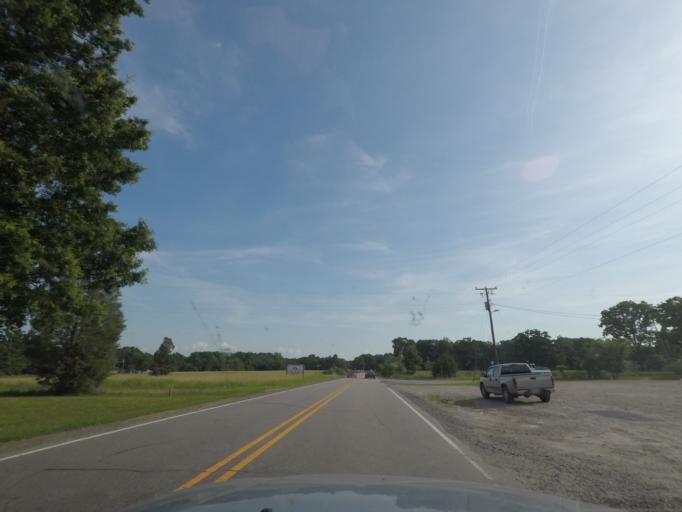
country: US
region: Virginia
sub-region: Mecklenburg County
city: Clarksville
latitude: 36.4999
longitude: -78.5413
